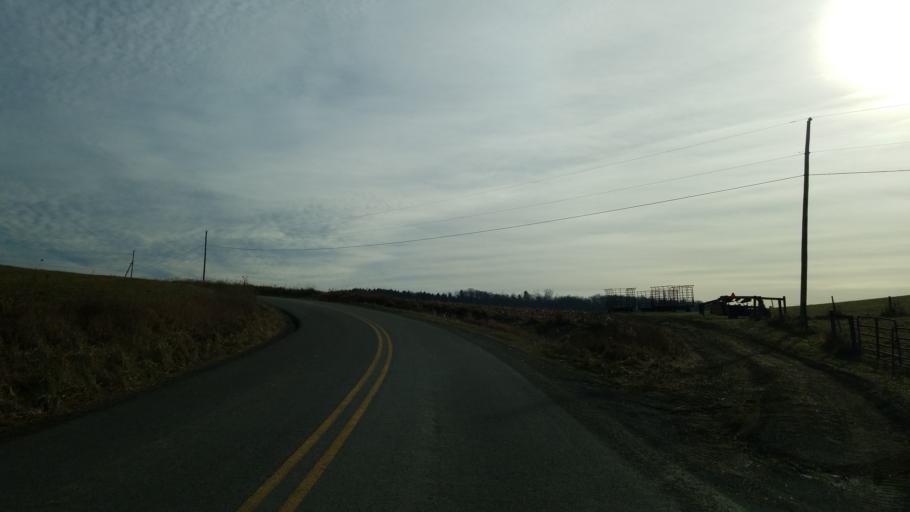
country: US
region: Pennsylvania
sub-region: Jefferson County
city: Albion
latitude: 40.9514
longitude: -78.9212
